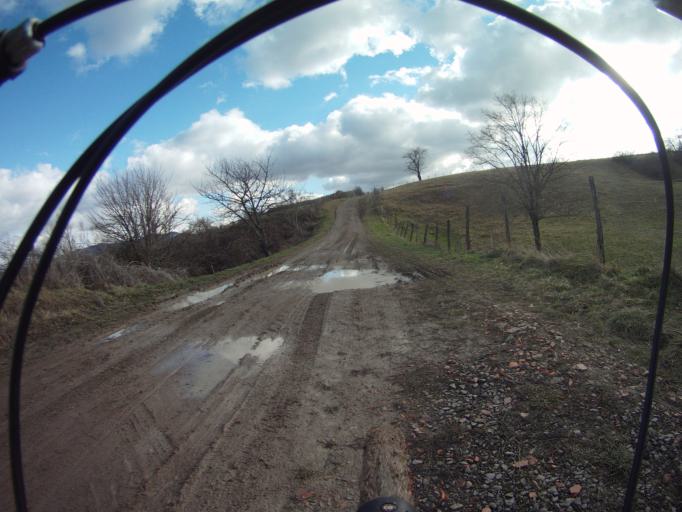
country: FR
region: Auvergne
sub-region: Departement du Puy-de-Dome
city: Perignat-les-Sarlieve
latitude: 45.7216
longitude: 3.1515
